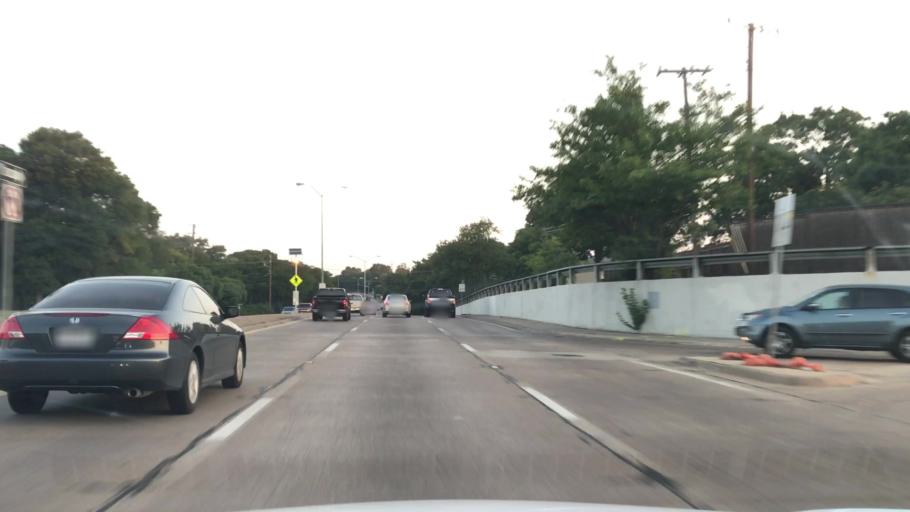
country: US
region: Texas
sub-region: Dallas County
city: Highland Park
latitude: 32.8177
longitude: -96.6898
